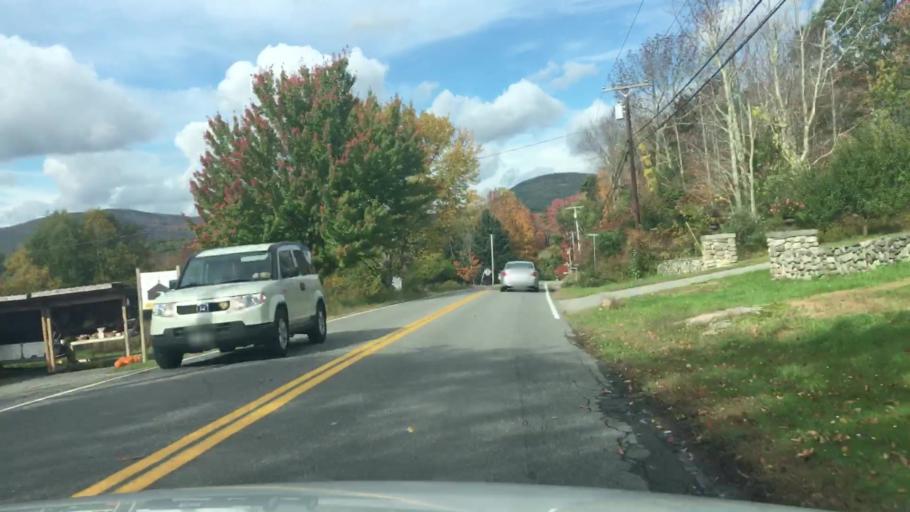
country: US
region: Maine
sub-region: Knox County
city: Camden
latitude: 44.2090
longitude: -69.0903
